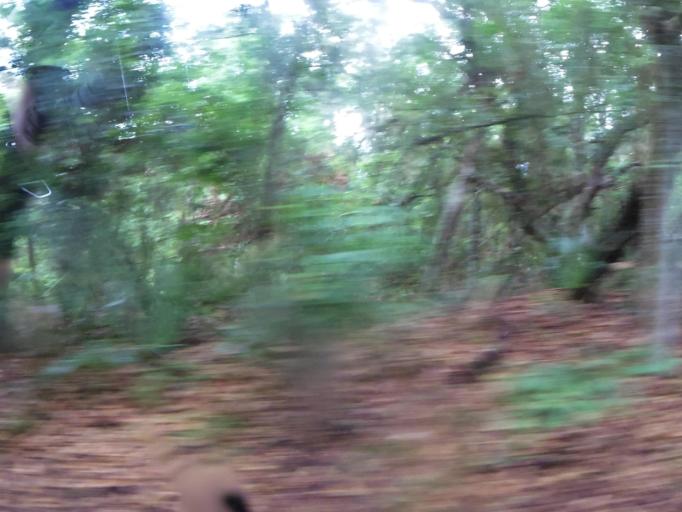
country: US
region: Florida
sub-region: Nassau County
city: Fernandina Beach
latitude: 30.6917
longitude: -81.4385
